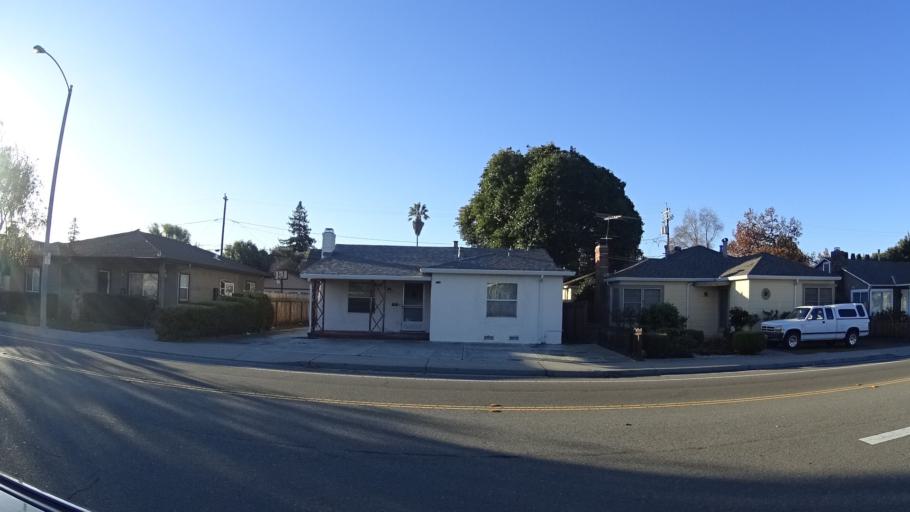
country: US
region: California
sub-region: Santa Clara County
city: Sunnyvale
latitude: 37.3704
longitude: -122.0311
